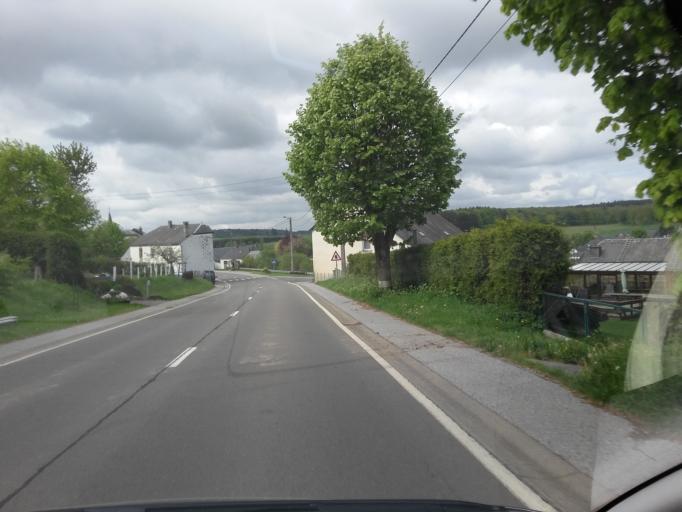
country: BE
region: Wallonia
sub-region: Province du Luxembourg
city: Neufchateau
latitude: 49.8439
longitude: 5.3779
